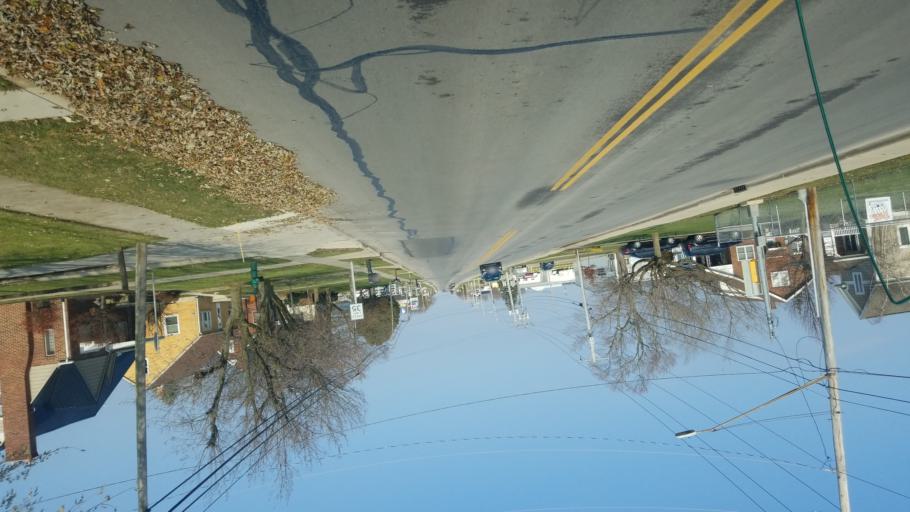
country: US
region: Ohio
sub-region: Mercer County
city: Coldwater
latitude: 40.4842
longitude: -84.6287
